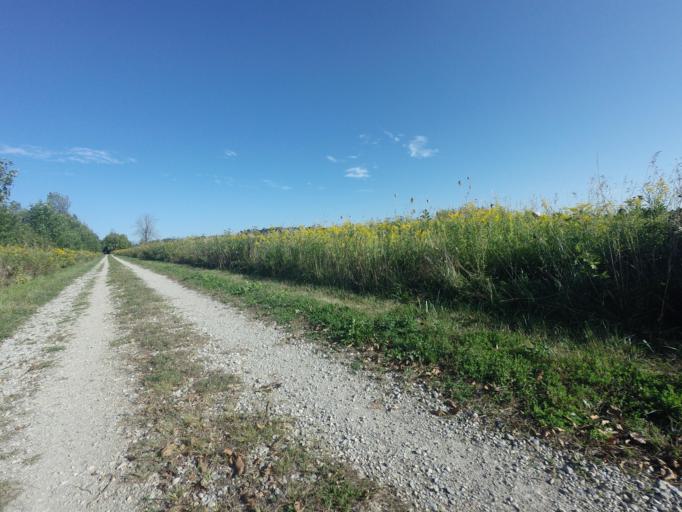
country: CA
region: Ontario
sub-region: Wellington County
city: Guelph
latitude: 43.6599
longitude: -80.4285
